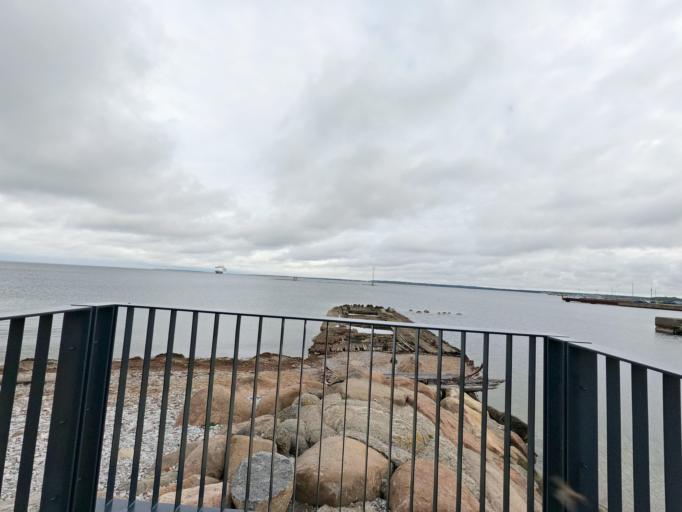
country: EE
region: Harju
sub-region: Tallinna linn
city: Tallinn
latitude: 59.4495
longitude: 24.7487
